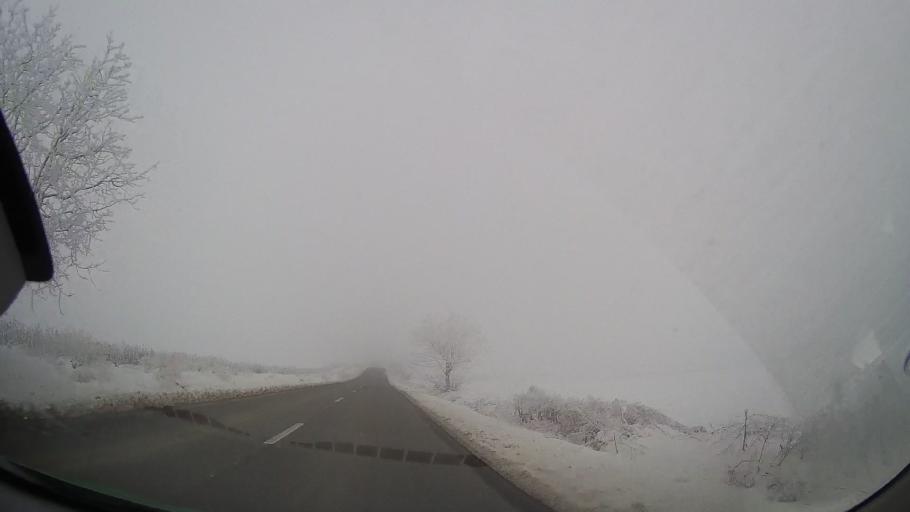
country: RO
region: Iasi
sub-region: Comuna Mogosesti-Siret
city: Mogosesti-Siret
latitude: 47.1522
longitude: 26.7773
